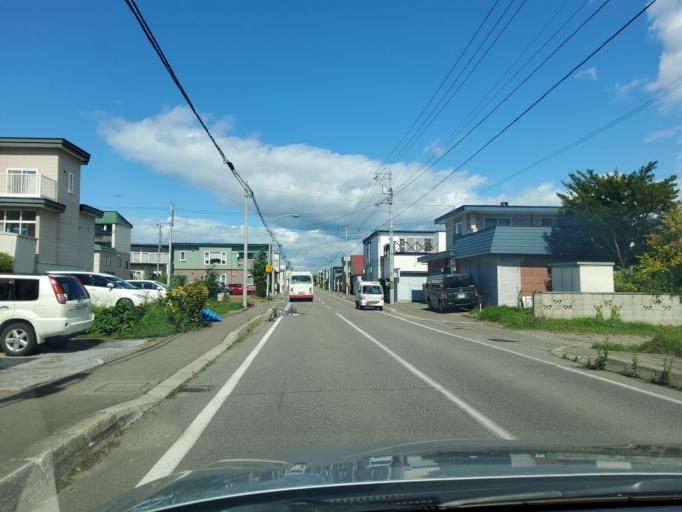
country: JP
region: Hokkaido
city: Obihiro
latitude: 42.9522
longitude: 143.2026
